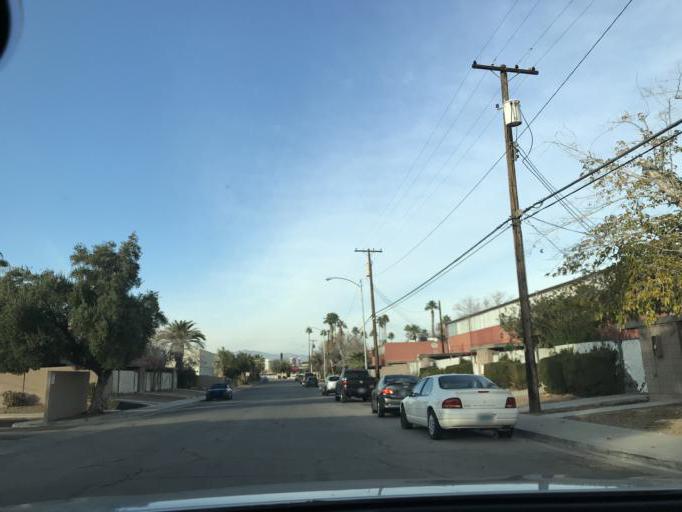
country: US
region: Nevada
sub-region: Clark County
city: Winchester
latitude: 36.1420
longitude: -115.1456
